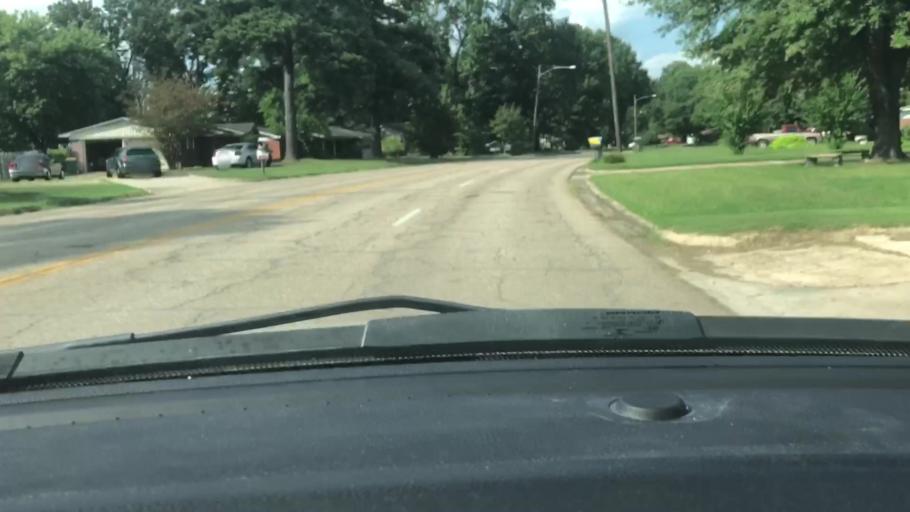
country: US
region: Texas
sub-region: Bowie County
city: Wake Village
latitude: 33.4031
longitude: -94.0801
